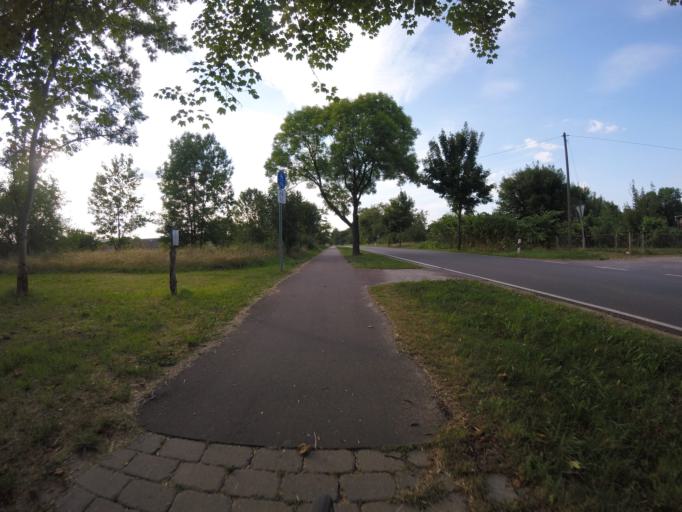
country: DE
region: Brandenburg
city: Altlandsberg
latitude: 52.5720
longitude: 13.7167
